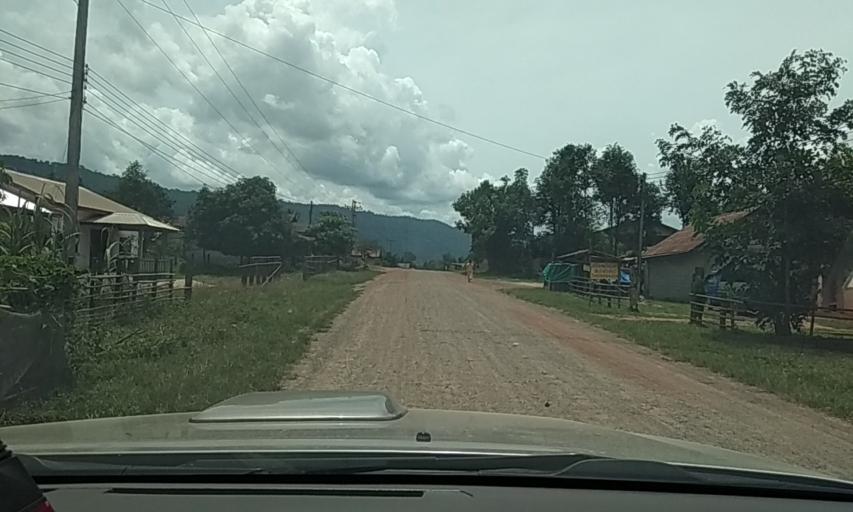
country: LA
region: Bolikhamxai
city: Ban Nahin
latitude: 18.1404
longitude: 104.7594
